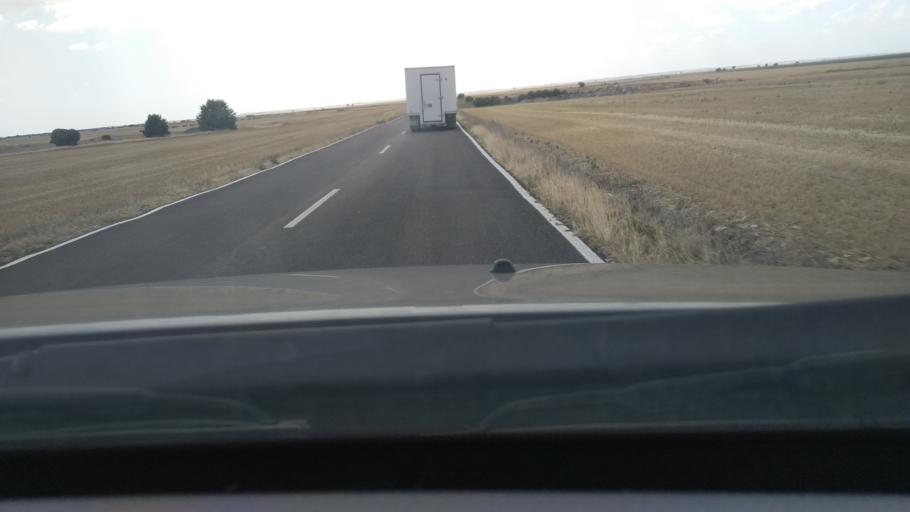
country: ES
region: Castille and Leon
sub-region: Provincia de Burgos
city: Iglesiarrubia
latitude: 41.9489
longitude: -3.8383
